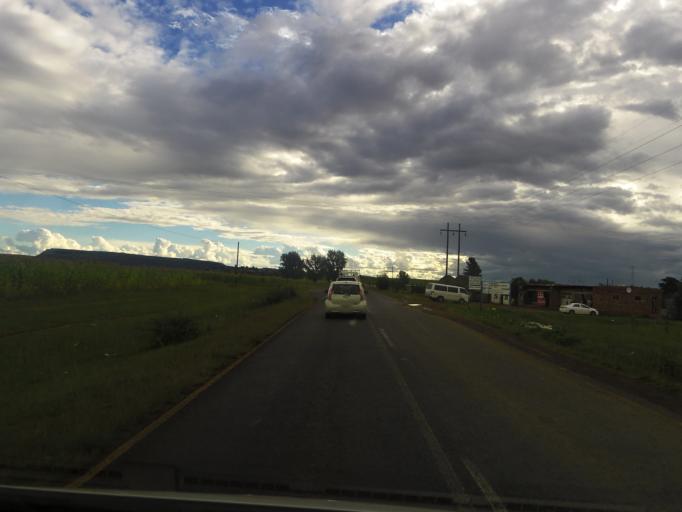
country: LS
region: Berea
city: Teyateyaneng
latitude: -29.1798
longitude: 27.6241
